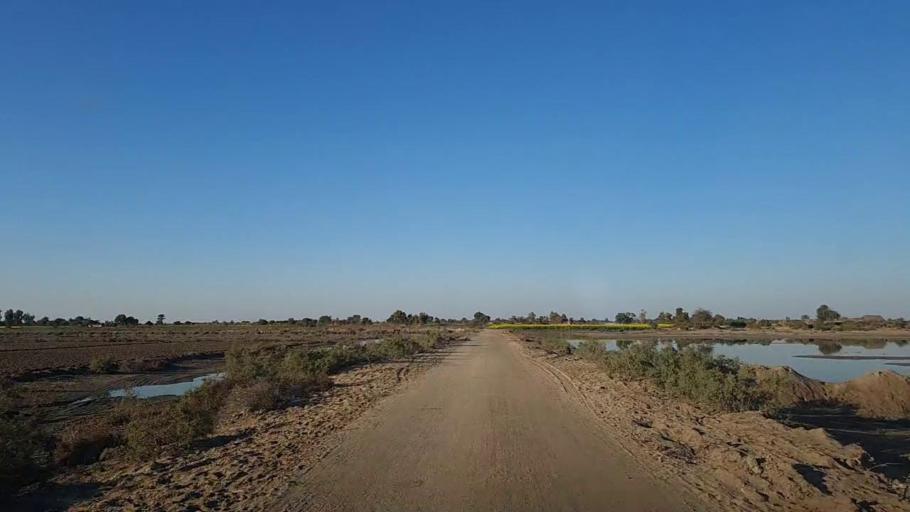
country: PK
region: Sindh
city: Sanghar
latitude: 26.1459
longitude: 68.9265
